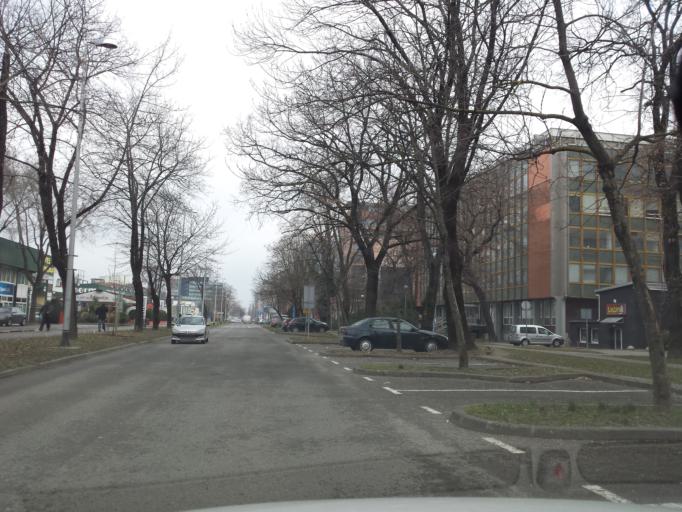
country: HR
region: Grad Zagreb
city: Zagreb - Centar
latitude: 45.8046
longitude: 15.9967
